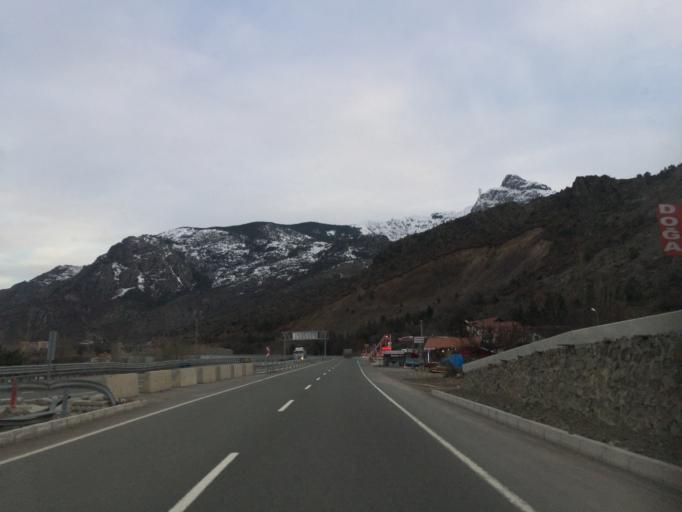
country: TR
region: Gumushane
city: Gumushkhane
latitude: 40.5078
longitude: 39.4221
